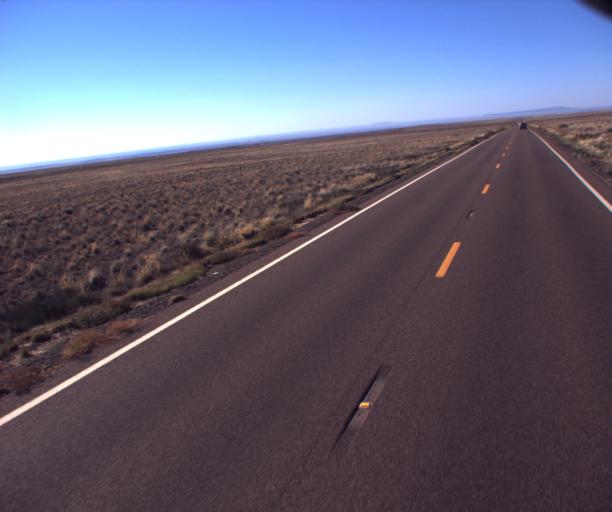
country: US
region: Arizona
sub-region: Navajo County
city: Joseph City
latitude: 35.1412
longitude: -110.4832
